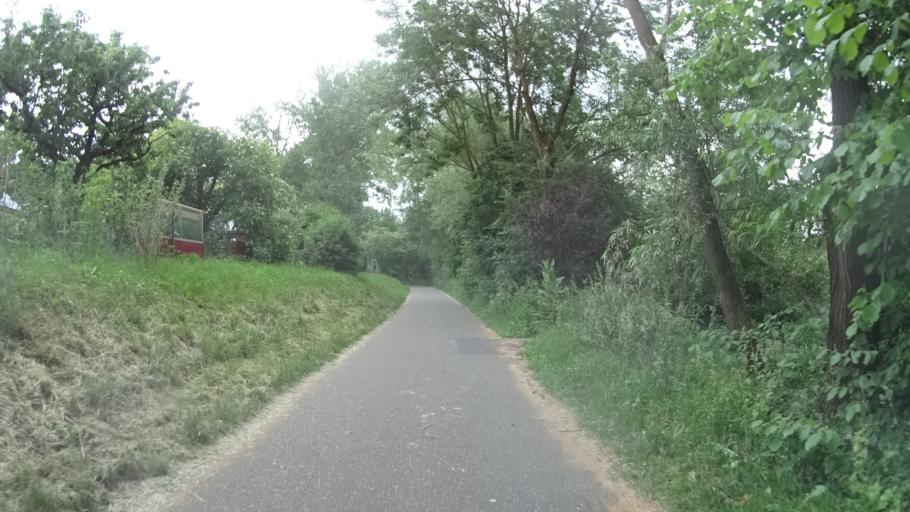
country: DE
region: Bavaria
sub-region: Upper Palatinate
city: Tegernheim
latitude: 49.0203
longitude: 12.1550
